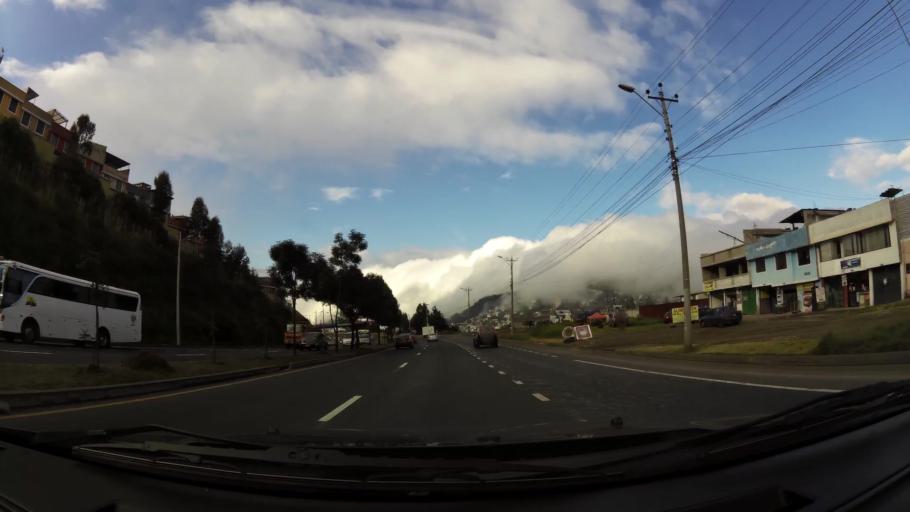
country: EC
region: Pichincha
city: Quito
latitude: -0.2383
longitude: -78.4910
